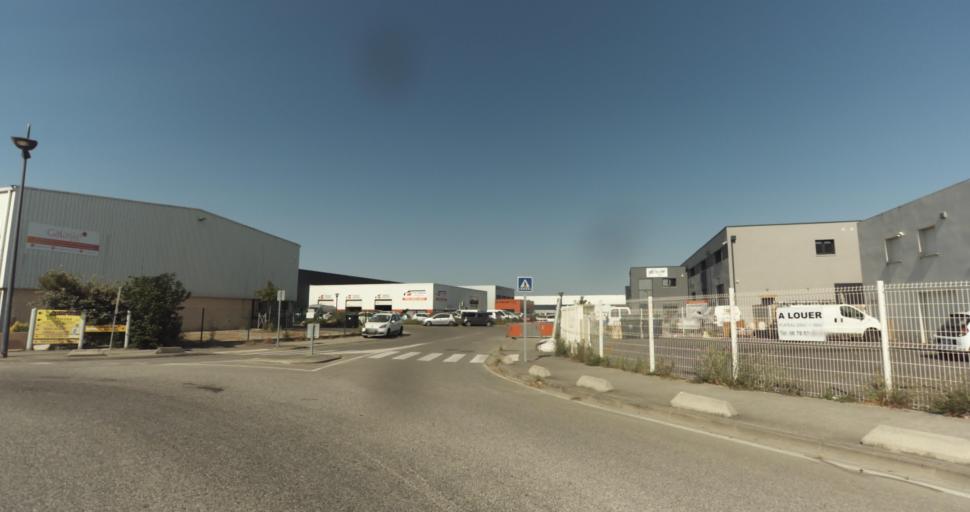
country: FR
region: Midi-Pyrenees
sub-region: Departement de la Haute-Garonne
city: Tournefeuille
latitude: 43.5924
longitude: 1.2997
